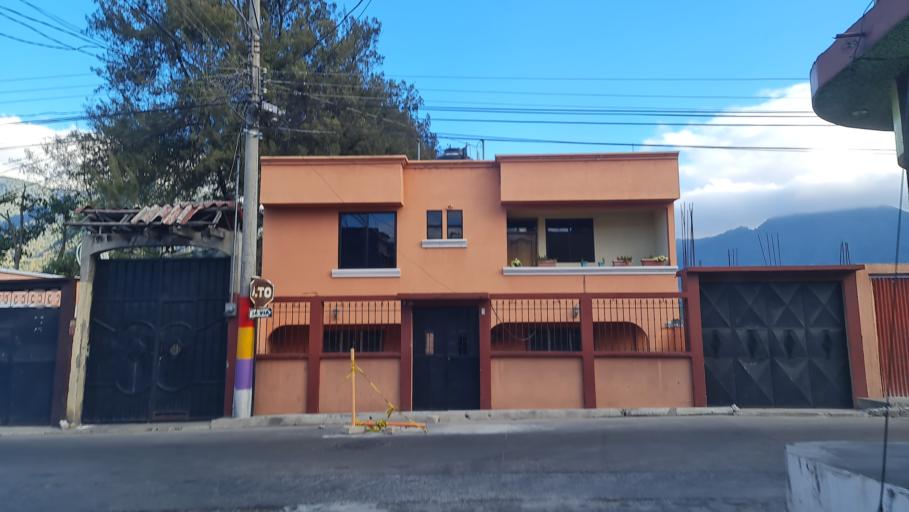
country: GT
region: San Marcos
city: San Pedro Sacatepequez
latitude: 14.9736
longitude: -91.7796
